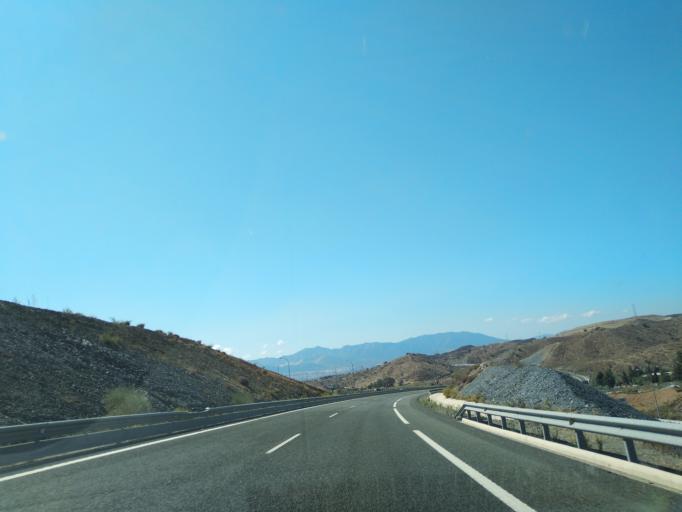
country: ES
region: Andalusia
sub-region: Provincia de Malaga
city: Malaga
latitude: 36.7539
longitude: -4.4893
